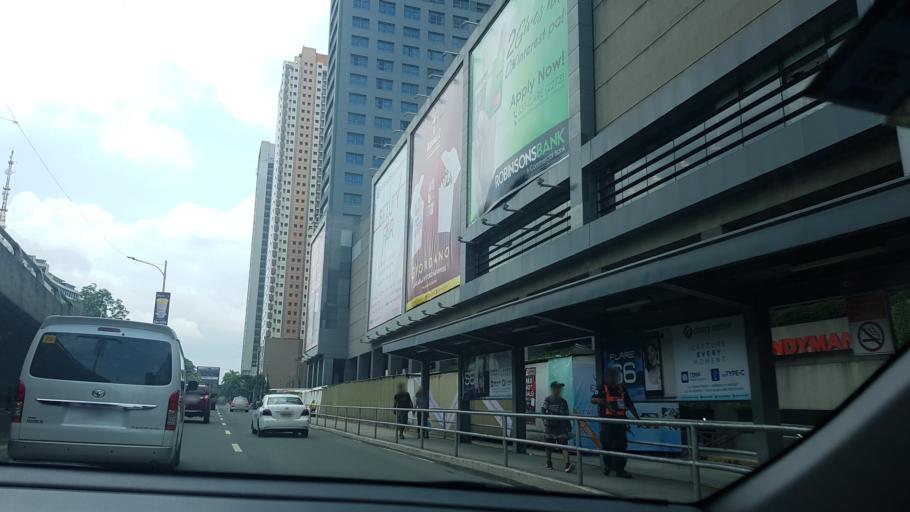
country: PH
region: Metro Manila
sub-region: Pasig
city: Pasig City
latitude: 14.5917
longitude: 121.0601
